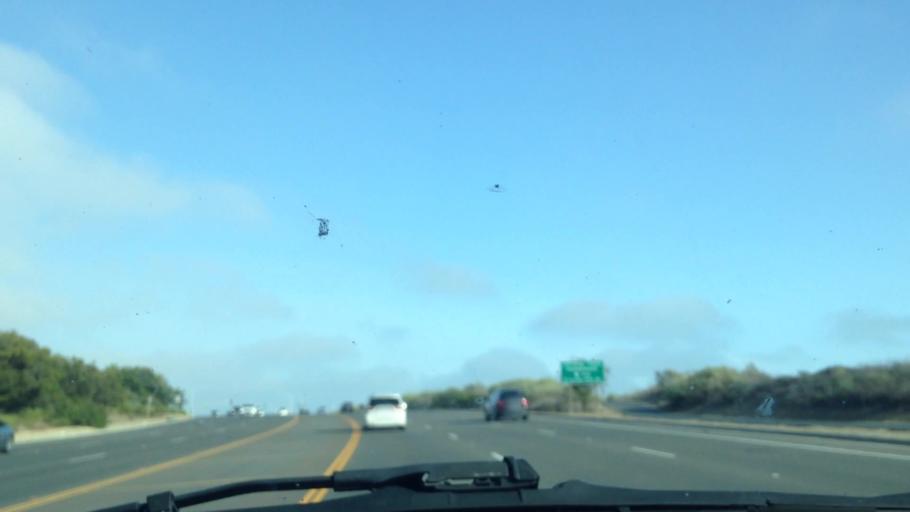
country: US
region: California
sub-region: Orange County
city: San Joaquin Hills
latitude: 33.5735
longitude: -117.8387
